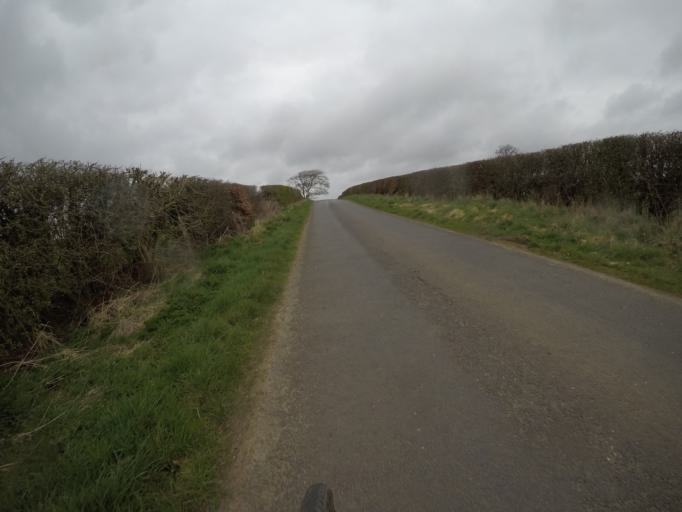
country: GB
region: Scotland
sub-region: East Ayrshire
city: Galston
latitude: 55.6191
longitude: -4.4351
